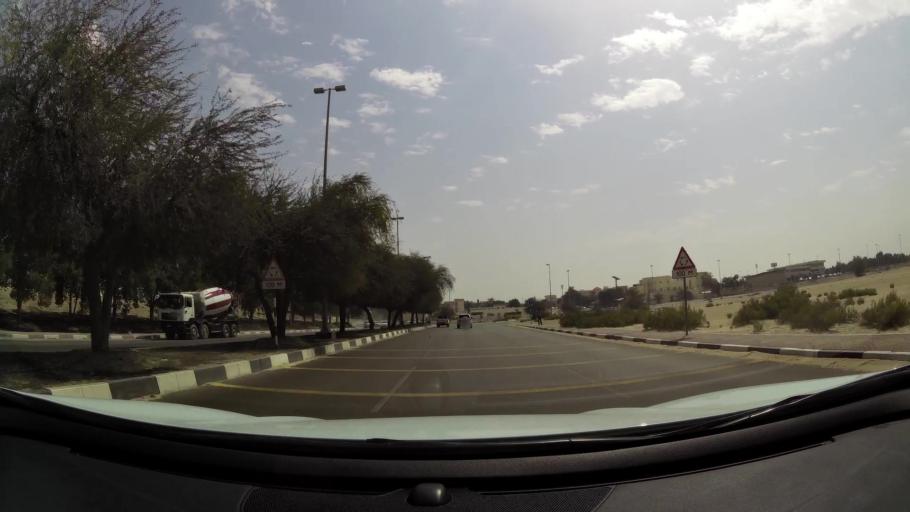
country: AE
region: Abu Dhabi
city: Abu Dhabi
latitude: 24.3023
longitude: 54.6249
